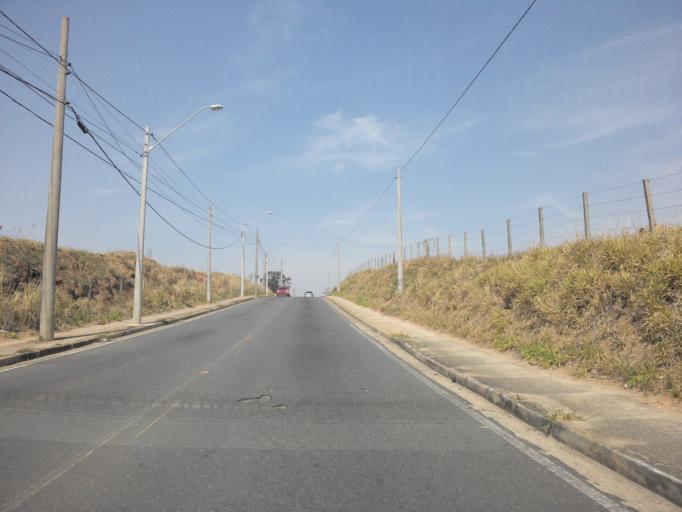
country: BR
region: Sao Paulo
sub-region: Hortolandia
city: Hortolandia
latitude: -22.9335
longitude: -47.1871
